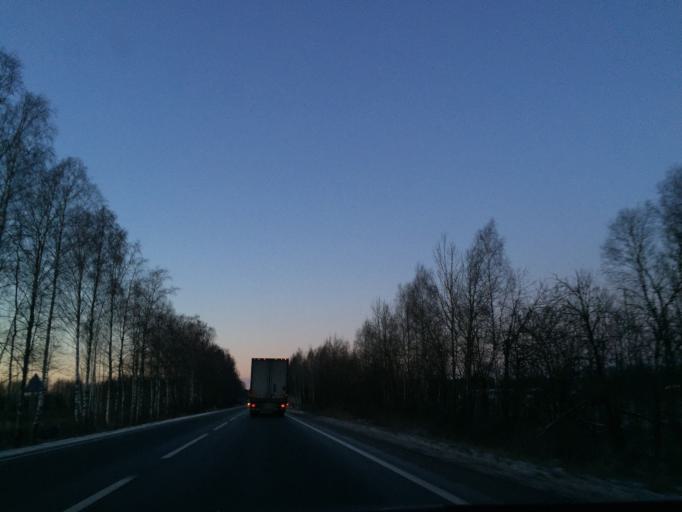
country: LV
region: Kekava
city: Balozi
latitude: 56.8746
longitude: 24.1688
